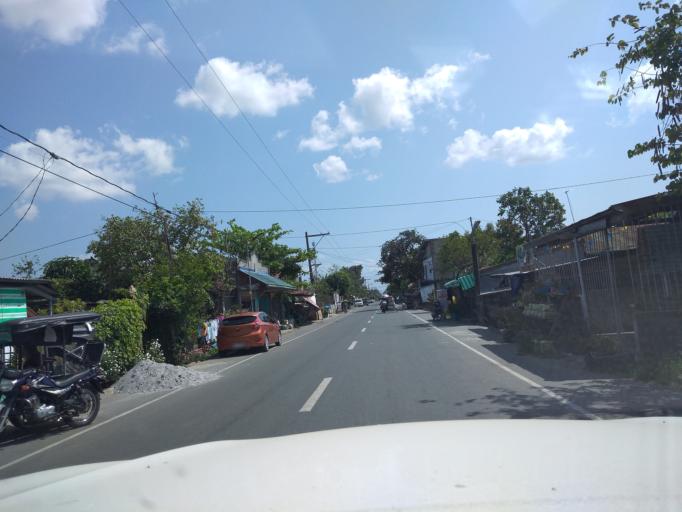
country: PH
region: Central Luzon
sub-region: Province of Pampanga
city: Bahay Pare
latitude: 15.0382
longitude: 120.8801
